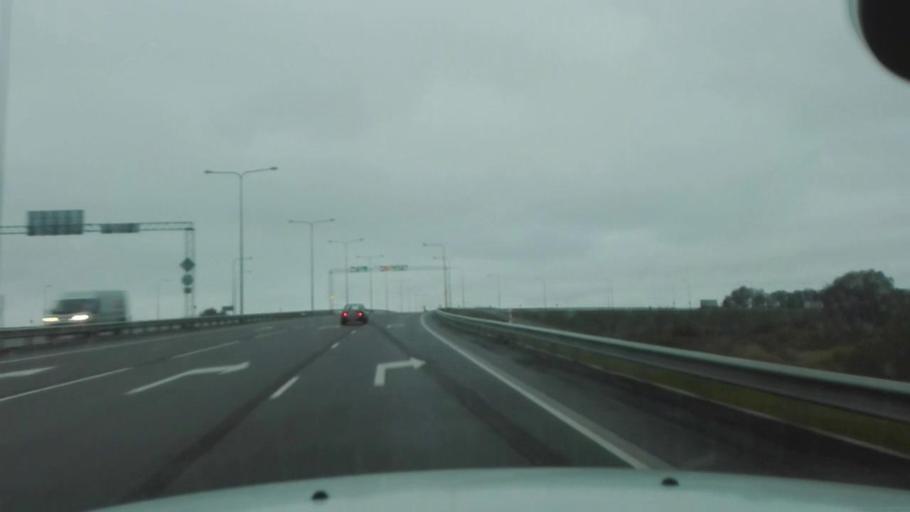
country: EE
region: Harju
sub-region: Joelaehtme vald
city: Loo
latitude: 59.4567
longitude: 24.9811
